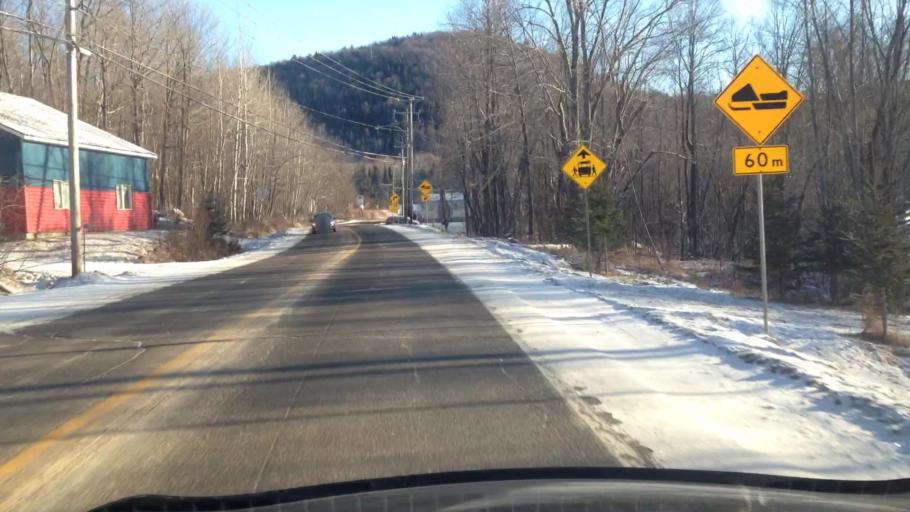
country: CA
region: Quebec
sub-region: Laurentides
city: Mont-Tremblant
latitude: 45.9483
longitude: -74.5549
